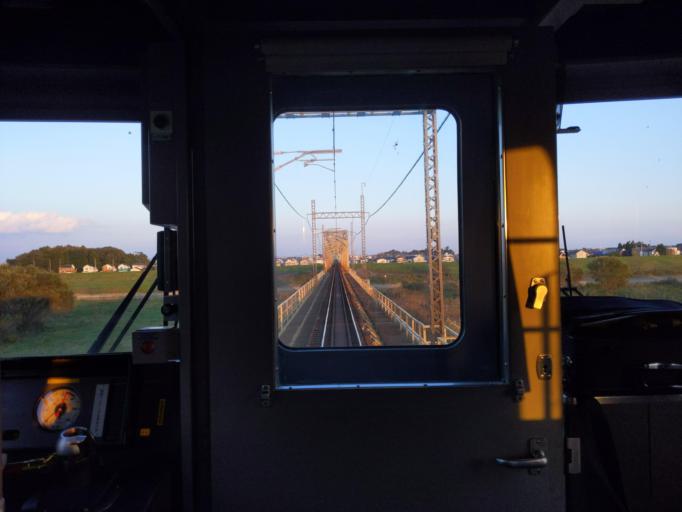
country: JP
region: Chiba
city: Noda
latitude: 35.9799
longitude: 139.8238
